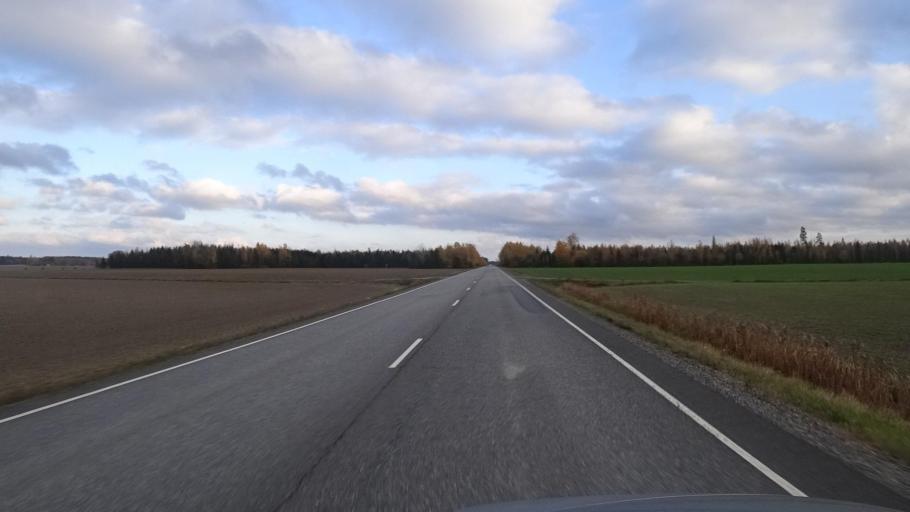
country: FI
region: Varsinais-Suomi
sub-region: Loimaa
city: Alastaro
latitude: 60.9072
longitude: 22.9222
